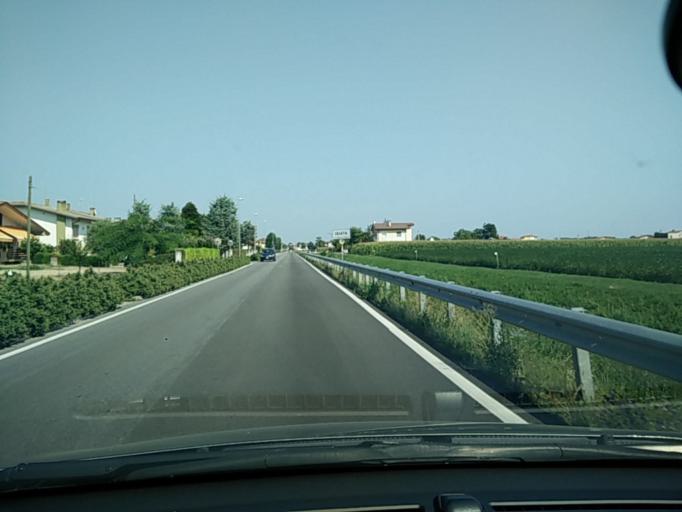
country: IT
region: Veneto
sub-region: Provincia di Venezia
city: Passarella
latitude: 45.6209
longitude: 12.6151
